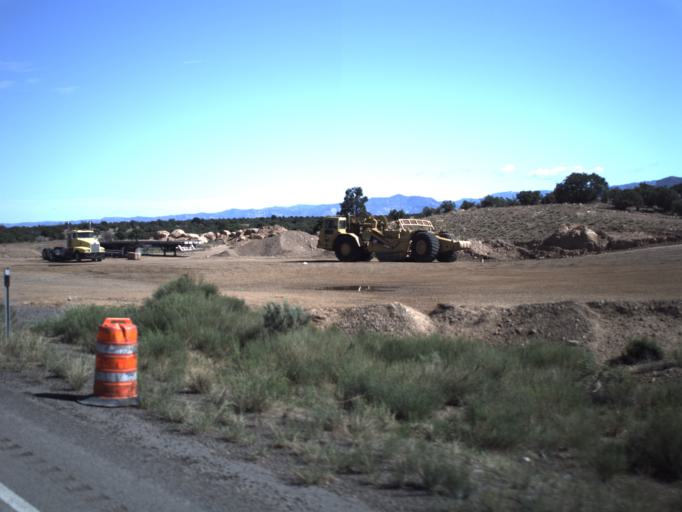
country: US
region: Utah
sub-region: Carbon County
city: East Carbon City
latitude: 39.4012
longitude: -110.4238
